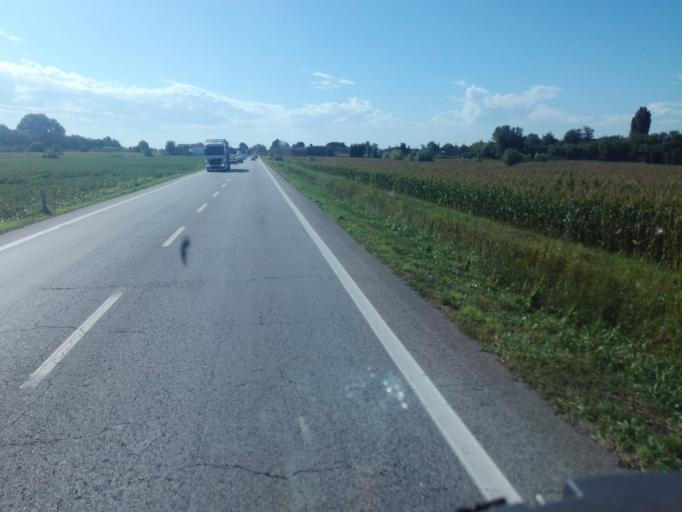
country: IT
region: Veneto
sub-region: Provincia di Venezia
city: Valli
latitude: 45.2417
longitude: 12.1451
